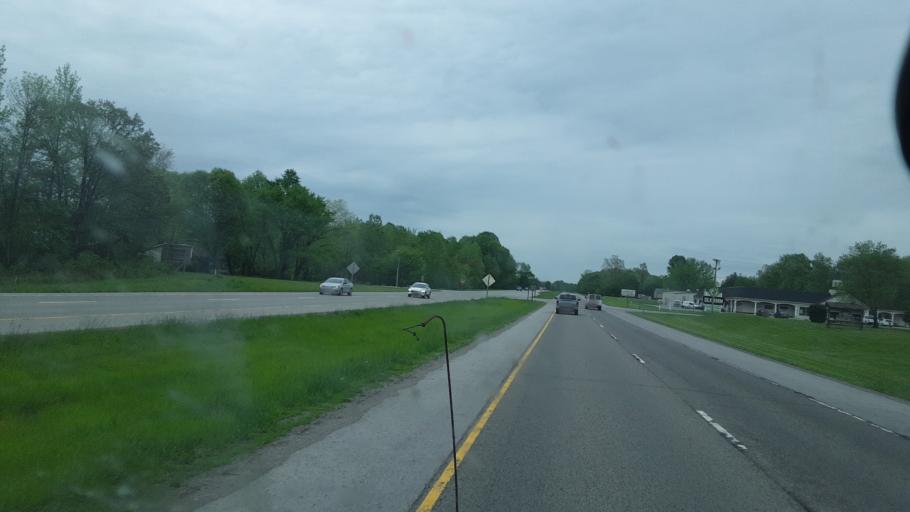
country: US
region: Illinois
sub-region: Jackson County
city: Murphysboro
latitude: 37.7654
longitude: -89.3136
